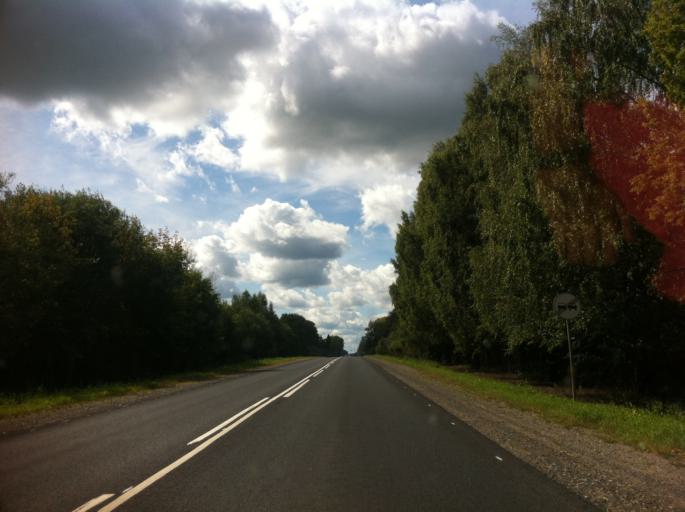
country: RU
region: Pskov
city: Izborsk
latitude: 57.7205
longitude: 27.9341
